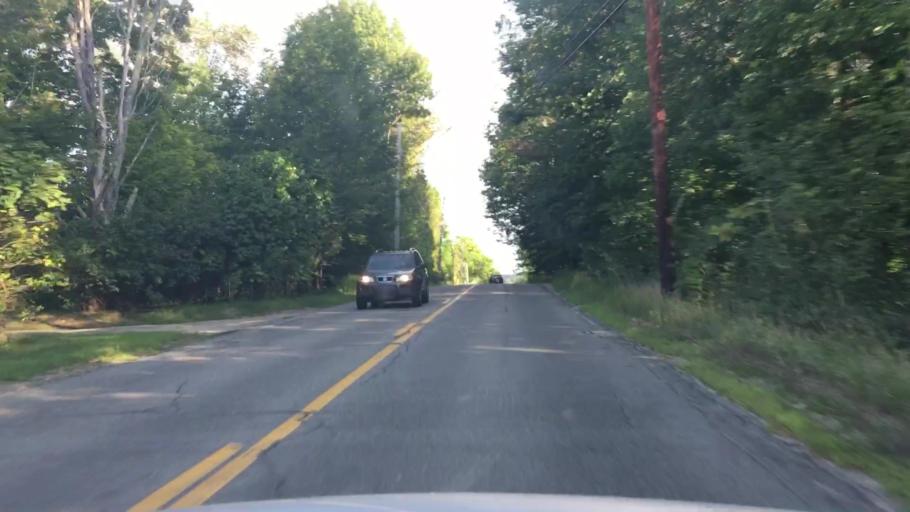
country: US
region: Maine
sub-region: Cumberland County
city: South Windham
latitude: 43.7347
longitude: -70.4147
